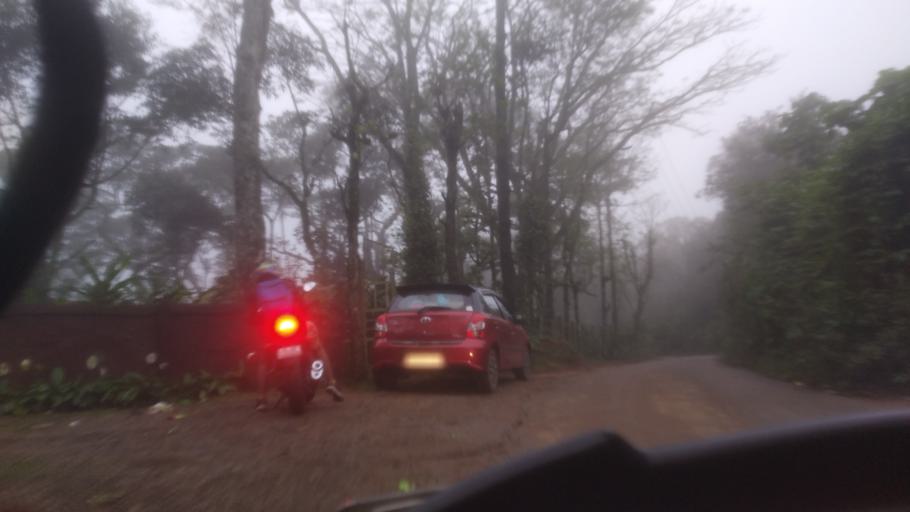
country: IN
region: Tamil Nadu
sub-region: Theni
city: Kombai
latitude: 9.8916
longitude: 77.2153
